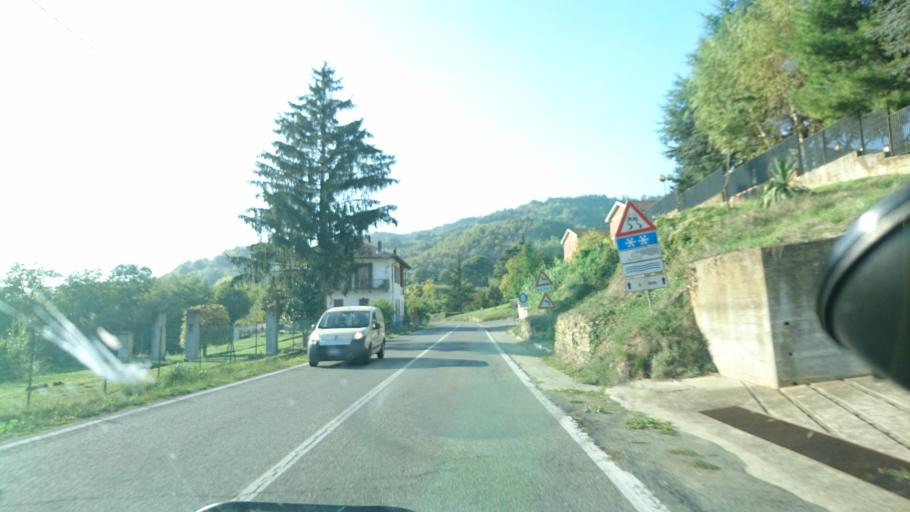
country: IT
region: Piedmont
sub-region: Provincia di Alessandria
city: Bistagno
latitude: 44.6628
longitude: 8.3655
